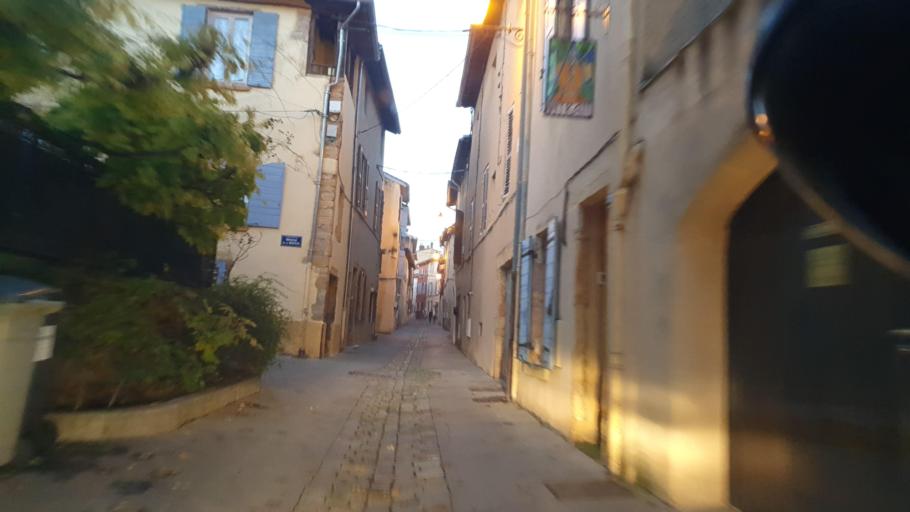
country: FR
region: Rhone-Alpes
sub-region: Departement du Rhone
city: Fontaines-sur-Saone
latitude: 45.8435
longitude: 4.8289
